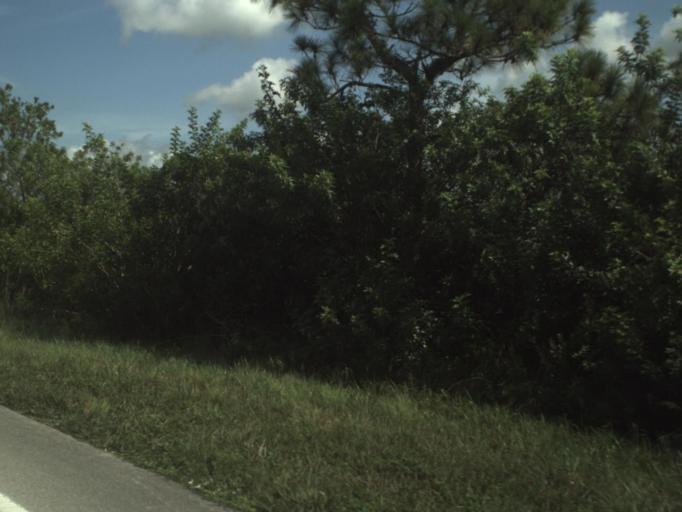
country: US
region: Florida
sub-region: Martin County
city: Indiantown
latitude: 26.9641
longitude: -80.3830
